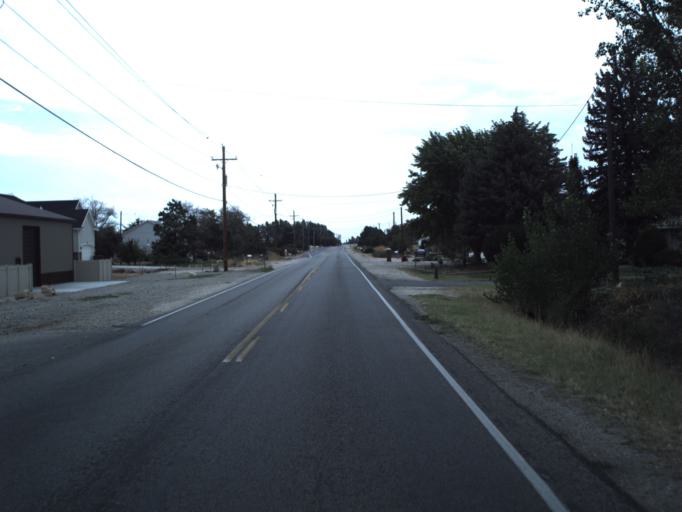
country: US
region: Utah
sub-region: Weber County
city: West Haven
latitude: 41.1974
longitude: -112.0932
